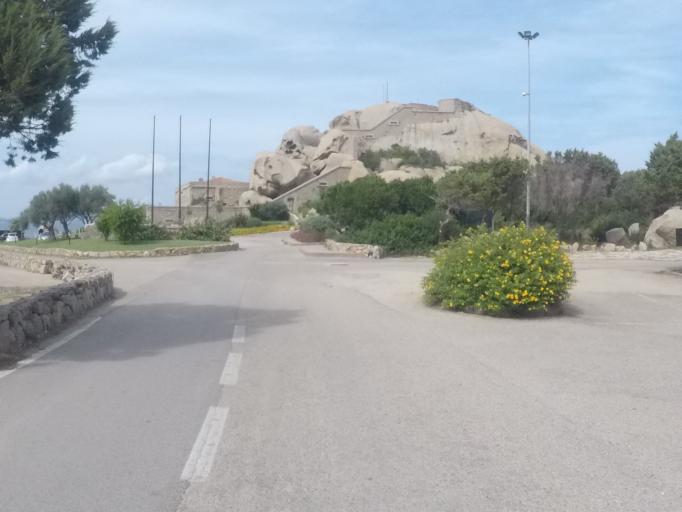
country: IT
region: Sardinia
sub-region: Provincia di Olbia-Tempio
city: Porto Cervo
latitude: 41.1412
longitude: 9.4680
